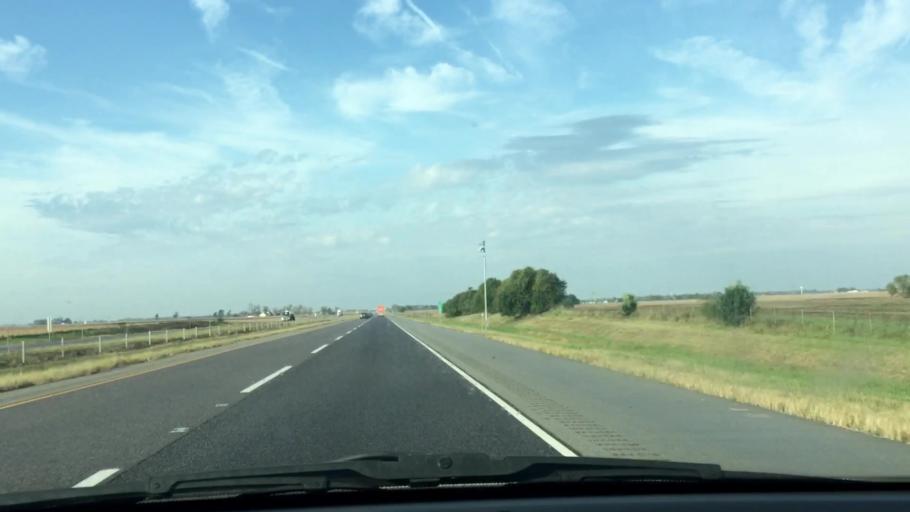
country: US
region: Illinois
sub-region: Lee County
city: Franklin Grove
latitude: 41.8481
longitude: -89.2395
